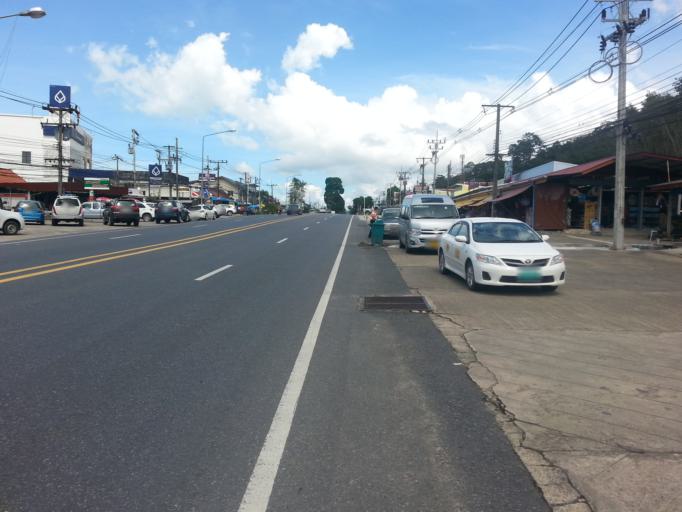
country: TH
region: Phangnga
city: Ban Khao Lak
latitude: 8.6459
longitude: 98.2518
